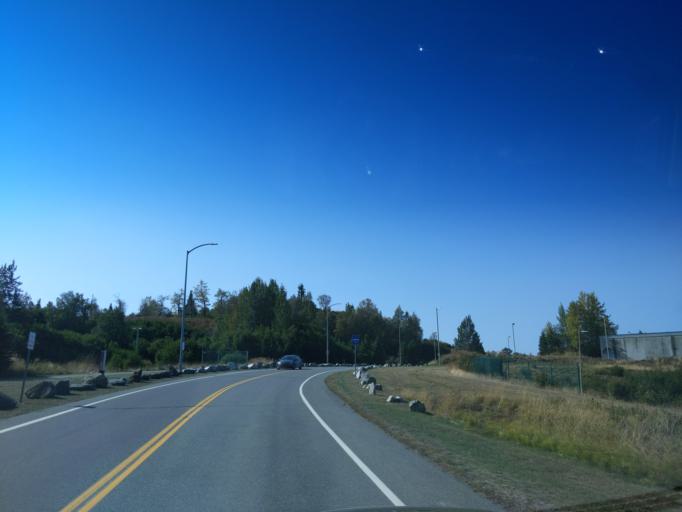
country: US
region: Alaska
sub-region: Anchorage Municipality
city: Anchorage
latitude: 61.1537
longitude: -150.0507
